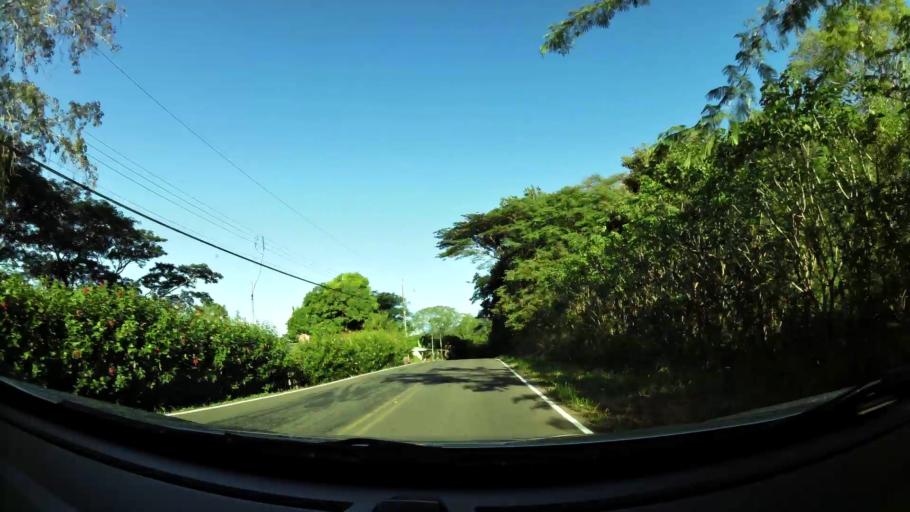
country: CR
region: Puntarenas
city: Miramar
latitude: 10.1341
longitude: -84.8424
